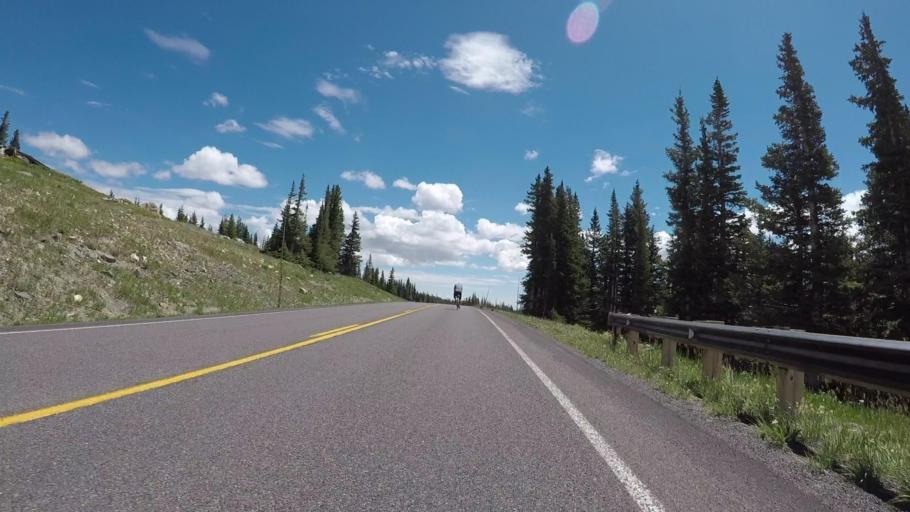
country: US
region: Wyoming
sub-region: Carbon County
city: Saratoga
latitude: 41.3511
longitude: -106.2745
